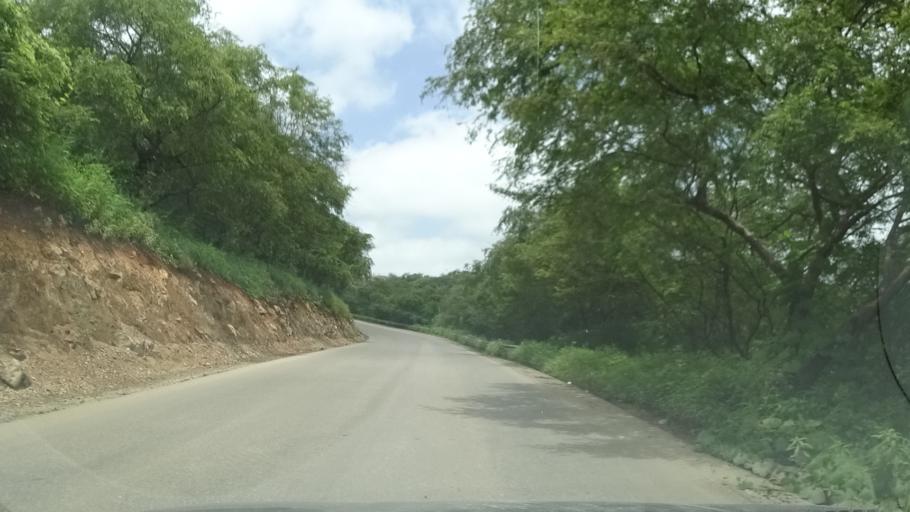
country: OM
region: Zufar
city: Salalah
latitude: 17.1786
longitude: 54.1629
